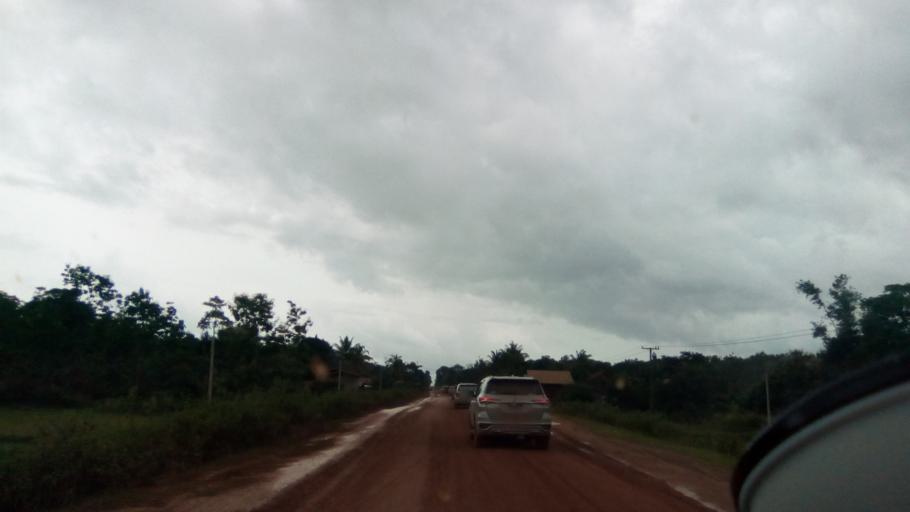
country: LA
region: Attapu
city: Attapu
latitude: 14.7493
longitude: 106.7003
